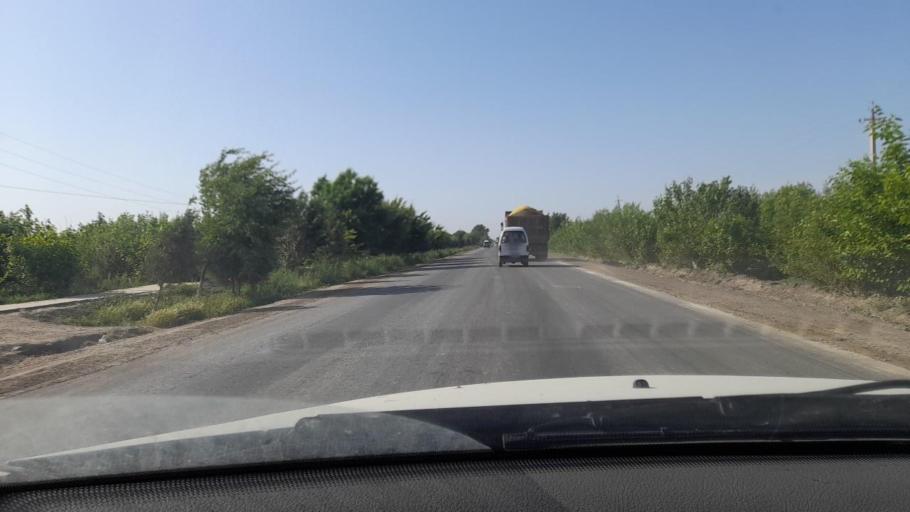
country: UZ
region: Bukhara
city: Romiton
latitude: 40.0530
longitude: 64.3282
